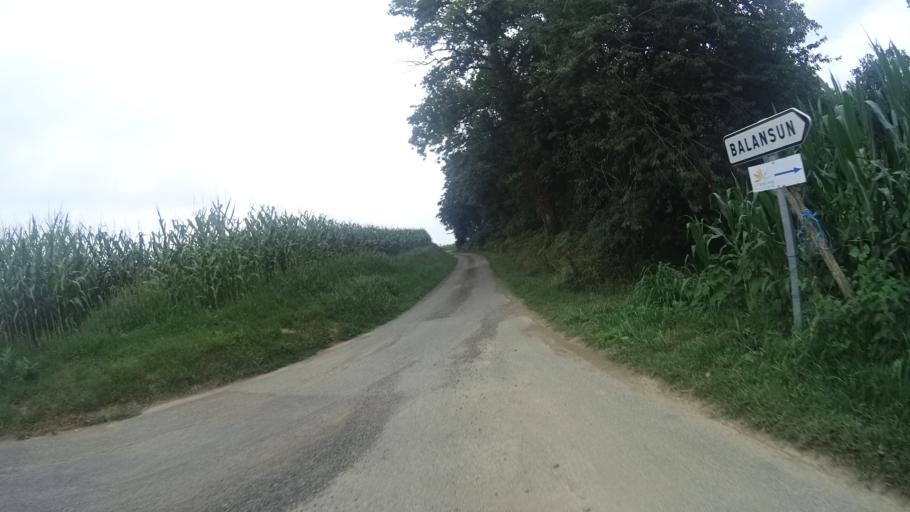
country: FR
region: Aquitaine
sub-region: Departement des Pyrenees-Atlantiques
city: Mont
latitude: 43.4979
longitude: -0.6895
